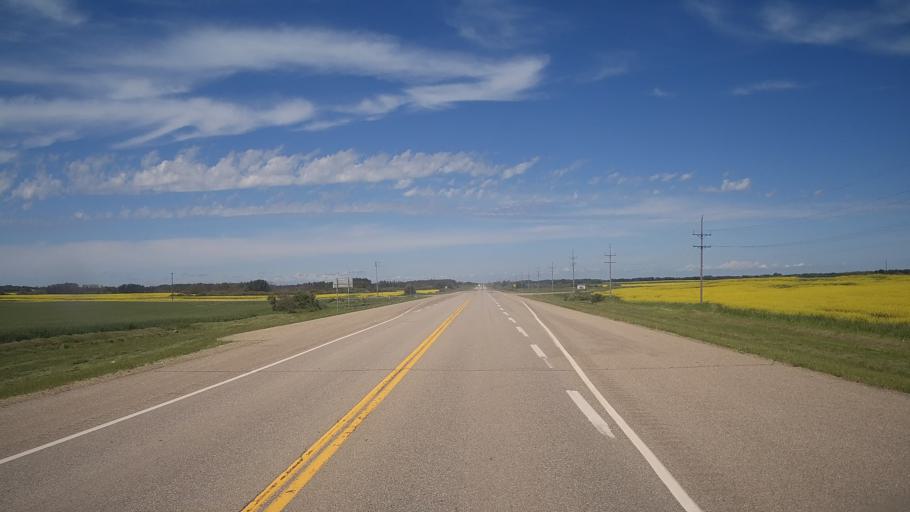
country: CA
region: Saskatchewan
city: Langenburg
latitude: 50.6364
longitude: -101.2759
